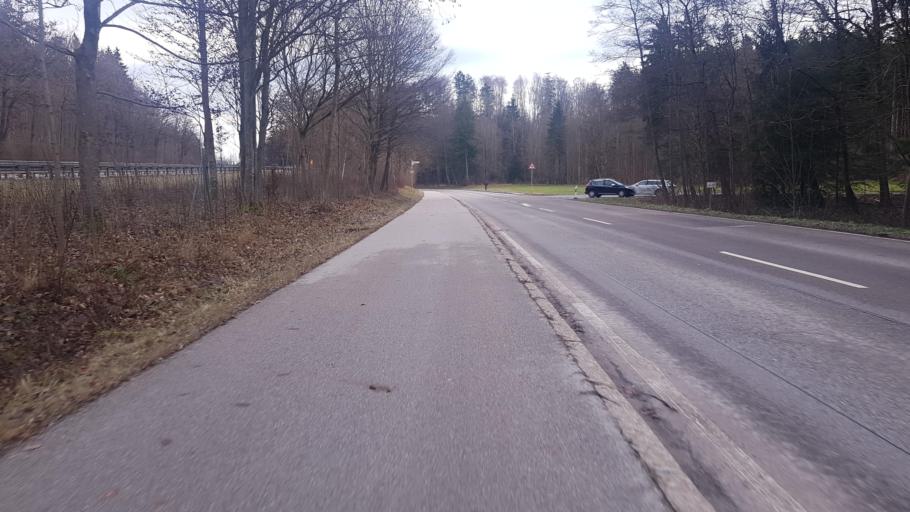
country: DE
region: Bavaria
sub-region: Upper Bavaria
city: Starnberg
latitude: 48.0043
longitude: 11.3937
